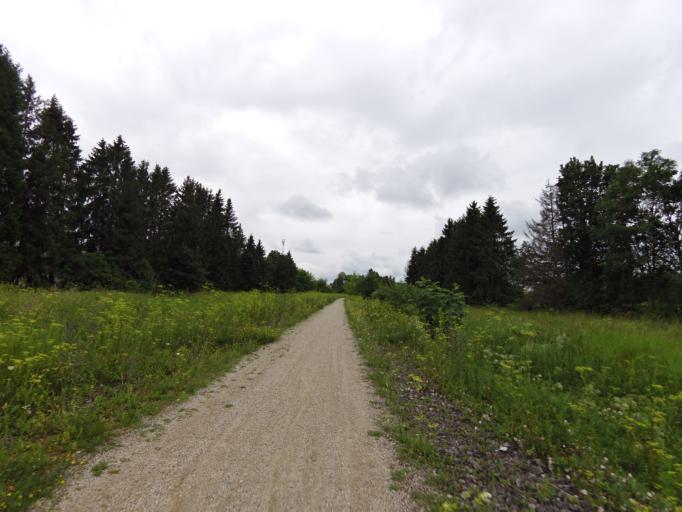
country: EE
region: Harju
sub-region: Nissi vald
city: Turba
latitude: 58.9998
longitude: 24.0591
